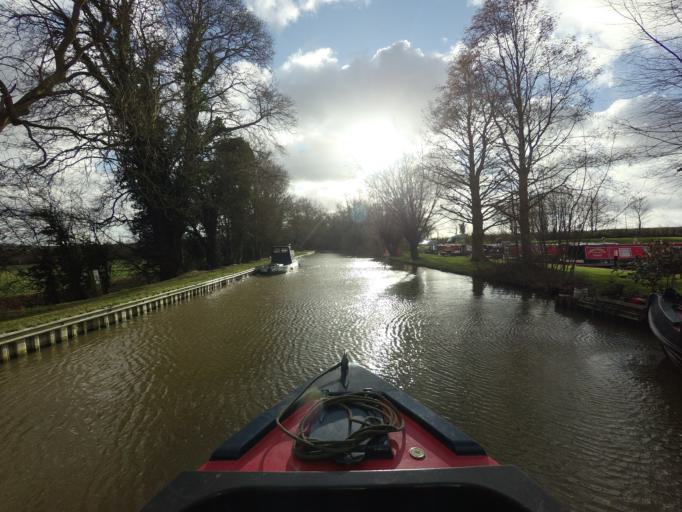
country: GB
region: England
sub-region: Northamptonshire
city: Long Buckby
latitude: 52.2903
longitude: -1.1219
